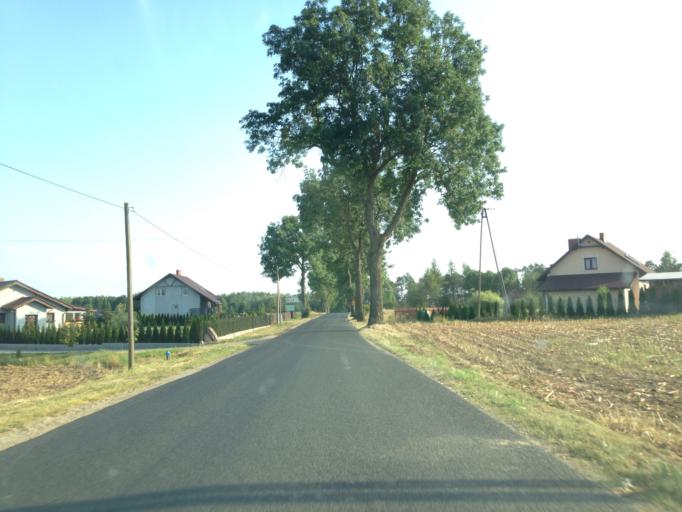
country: PL
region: Kujawsko-Pomorskie
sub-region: Powiat brodnicki
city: Brodnica
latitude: 53.3687
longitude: 19.3756
